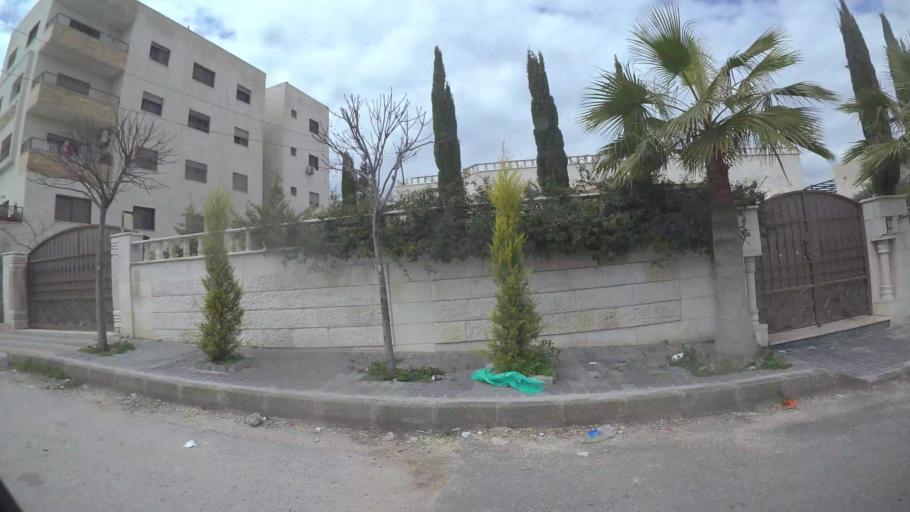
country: JO
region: Amman
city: Al Jubayhah
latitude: 32.0577
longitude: 35.8283
